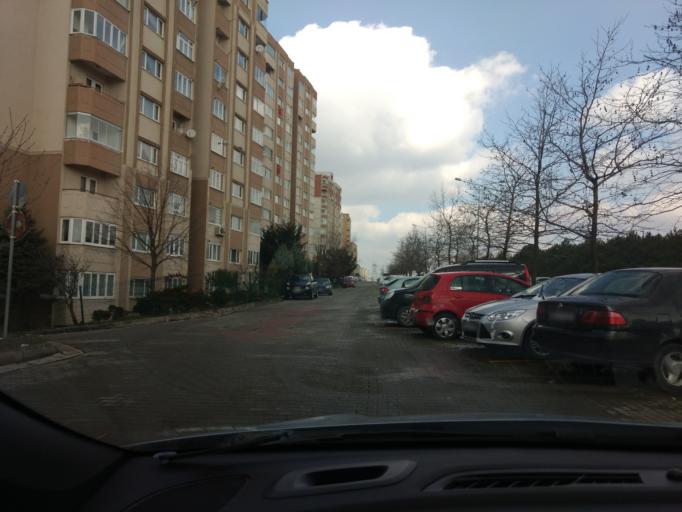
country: TR
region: Istanbul
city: Basaksehir
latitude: 41.1063
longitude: 28.8116
